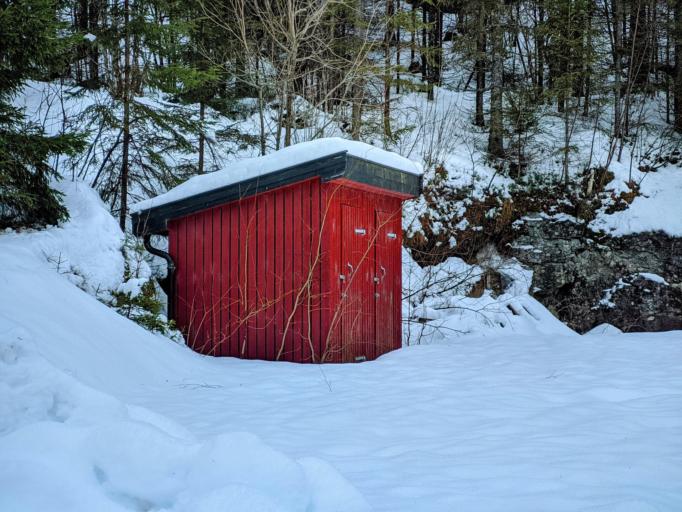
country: NO
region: Akershus
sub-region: Gjerdrum
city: Ask
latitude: 60.0514
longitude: 11.0154
